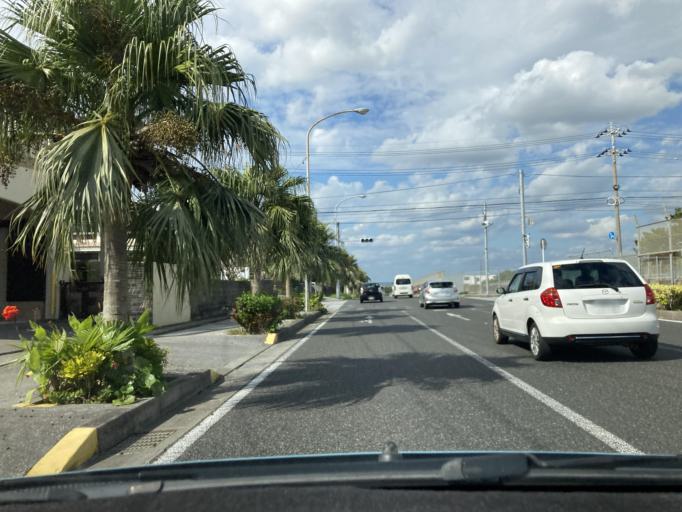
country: JP
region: Okinawa
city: Okinawa
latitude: 26.3263
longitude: 127.7866
